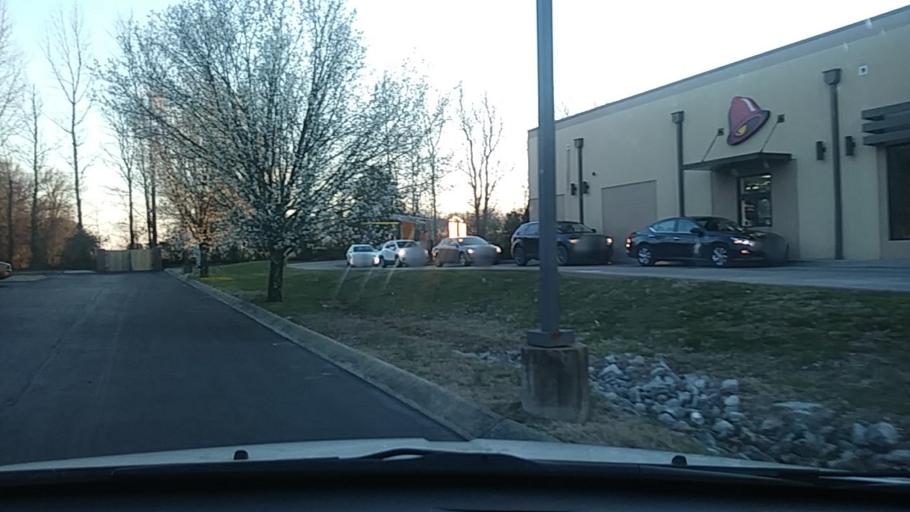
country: US
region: Tennessee
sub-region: Sumner County
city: Portland
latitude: 36.5769
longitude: -86.5259
